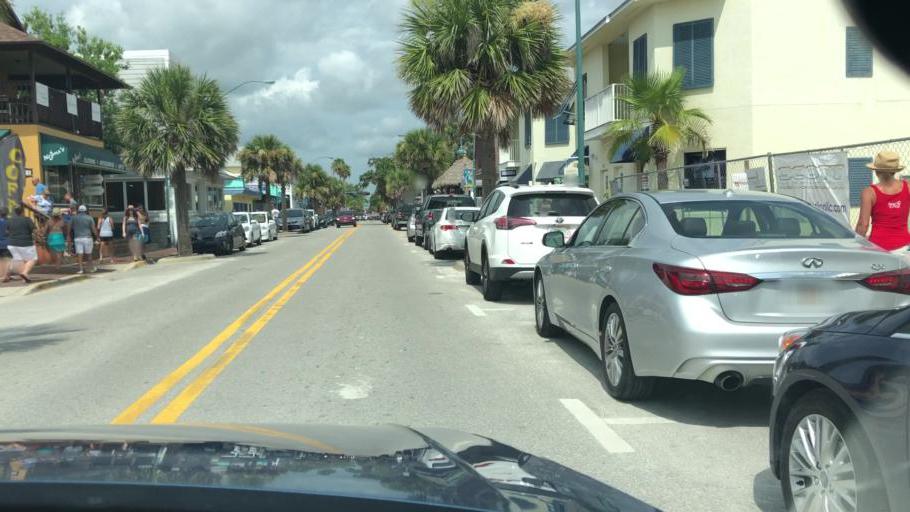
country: US
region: Florida
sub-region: Volusia County
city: New Smyrna Beach
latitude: 29.0386
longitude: -80.8989
